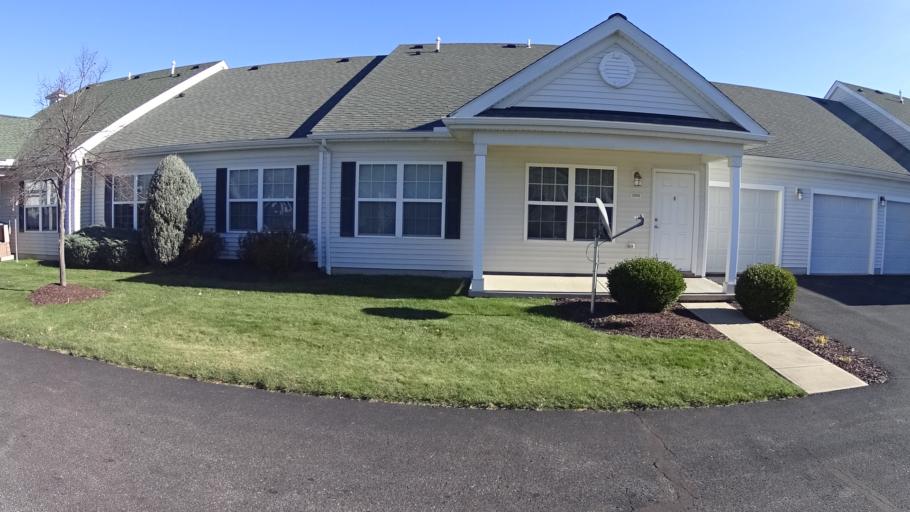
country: US
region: Ohio
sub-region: Lorain County
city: Avon Lake
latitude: 41.4951
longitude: -82.0631
